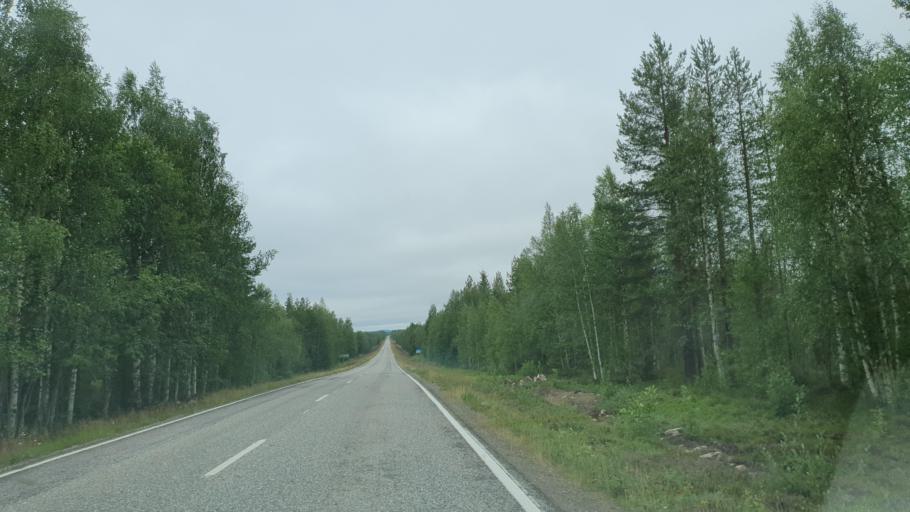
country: FI
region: Lapland
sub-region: Pohjois-Lappi
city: Sodankylae
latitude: 67.3877
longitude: 26.7980
